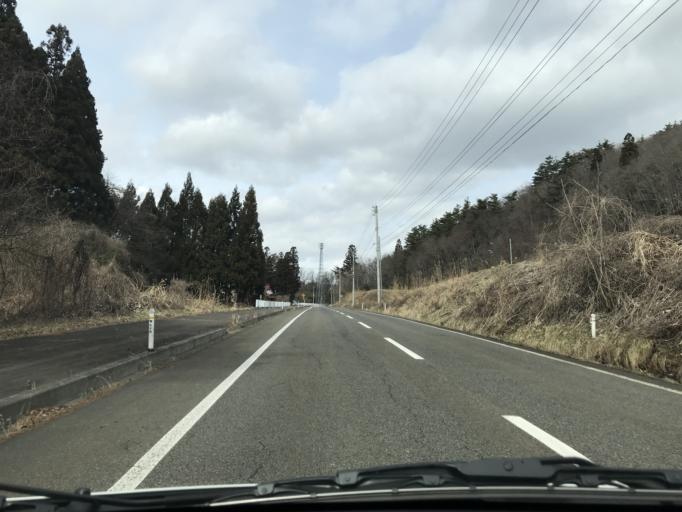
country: JP
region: Iwate
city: Tono
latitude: 39.2939
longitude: 141.3302
